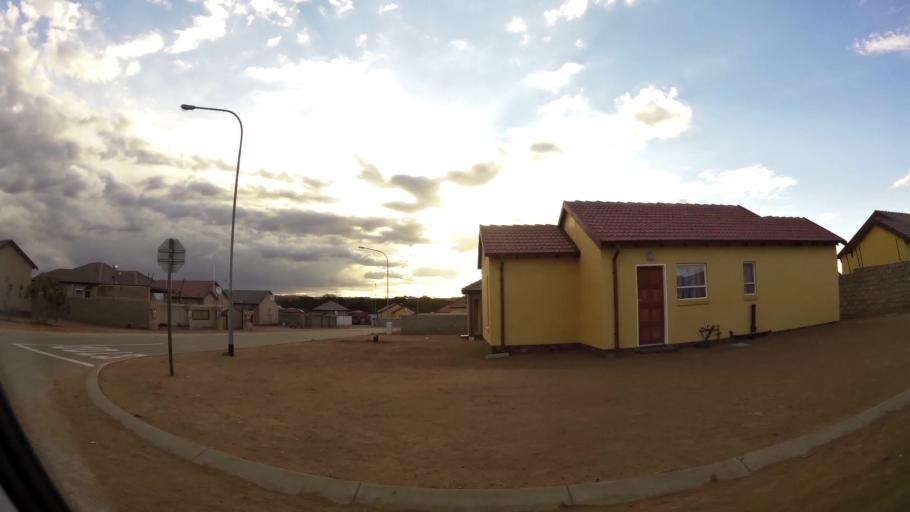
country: ZA
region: Limpopo
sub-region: Capricorn District Municipality
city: Polokwane
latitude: -23.9295
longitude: 29.4149
